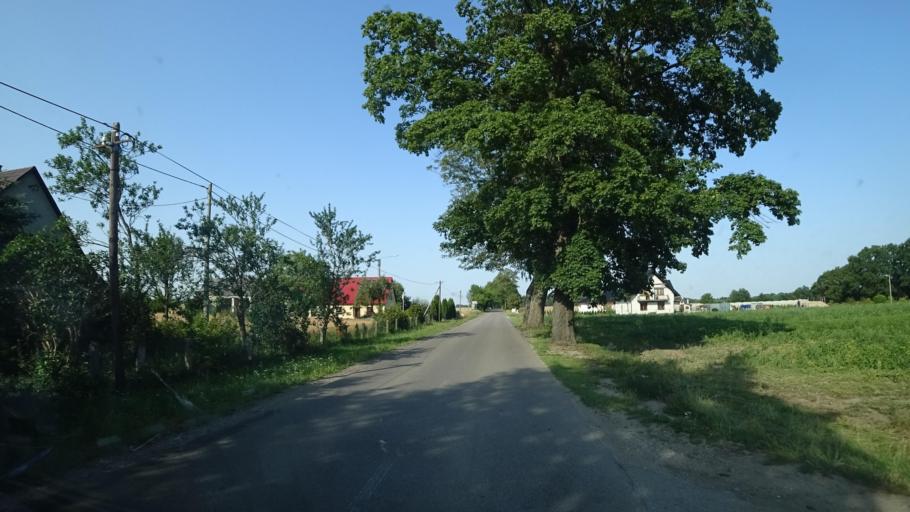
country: PL
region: Pomeranian Voivodeship
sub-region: Powiat czluchowski
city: Przechlewo
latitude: 53.8097
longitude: 17.3493
